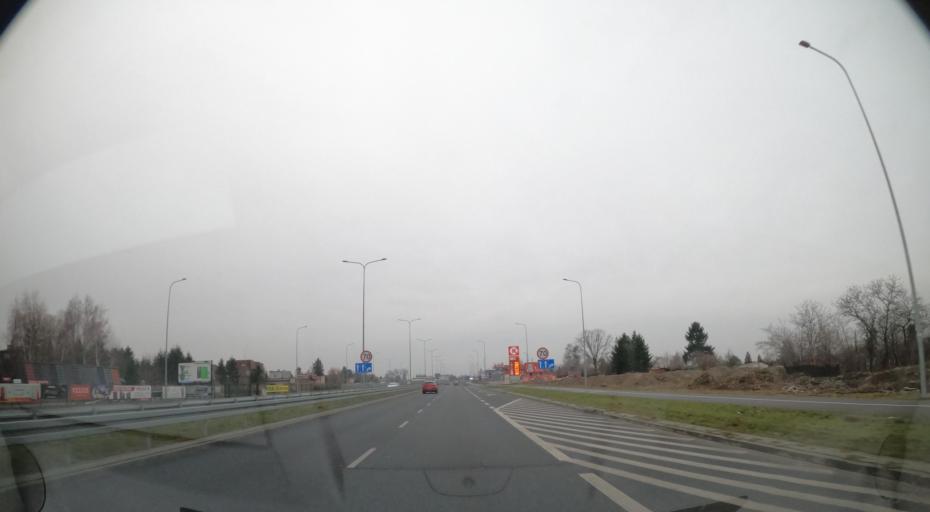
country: PL
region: Masovian Voivodeship
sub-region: Radom
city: Radom
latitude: 51.3935
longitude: 21.1954
